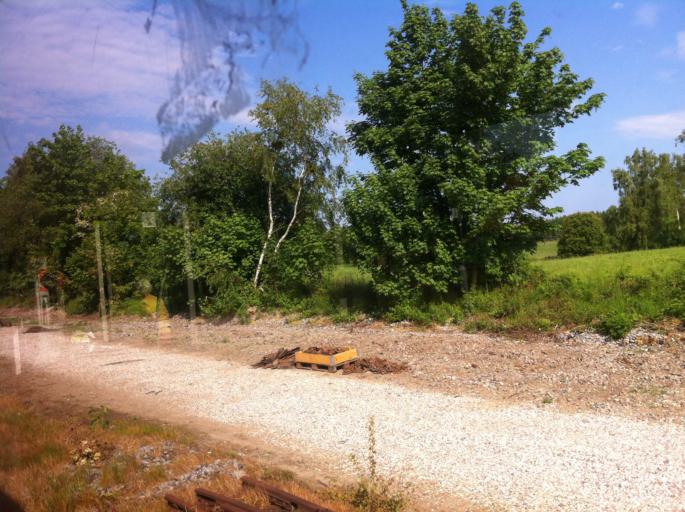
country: DK
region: Capital Region
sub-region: Gribskov Kommune
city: Gilleleje
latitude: 56.0984
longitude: 12.3563
